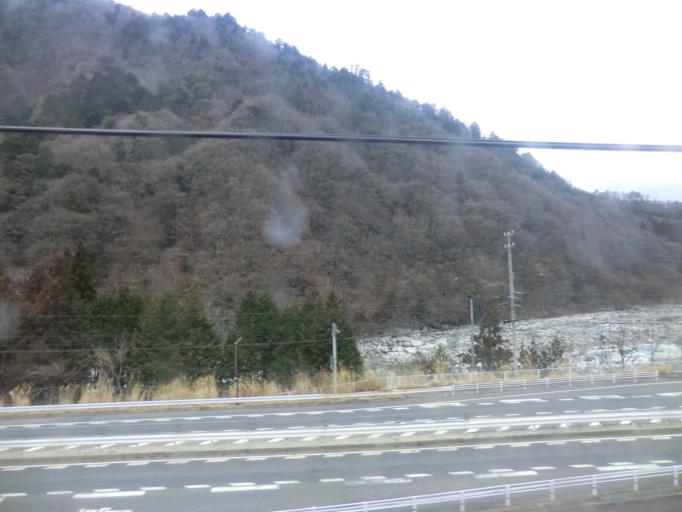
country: JP
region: Nagano
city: Iida
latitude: 35.7321
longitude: 137.7132
